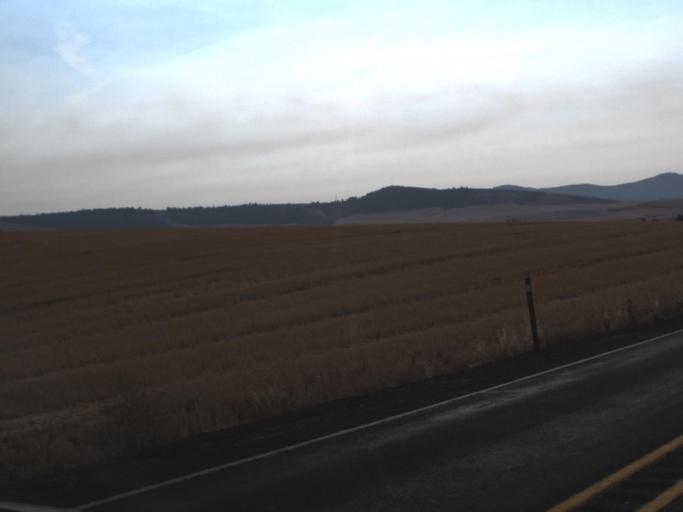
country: US
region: Idaho
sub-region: Benewah County
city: Plummer
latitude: 47.3277
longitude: -117.1878
